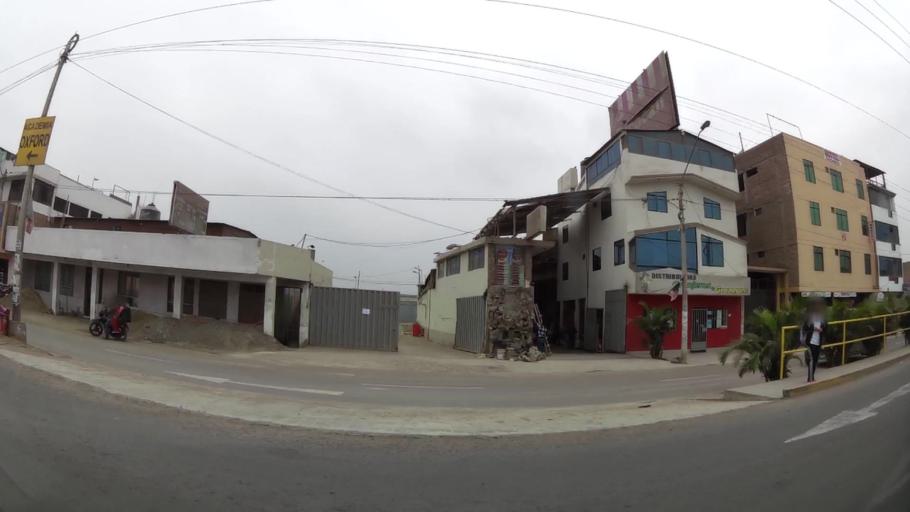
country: PE
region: Lima
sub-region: Lima
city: Punta Hermosa
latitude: -12.2963
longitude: -76.8508
